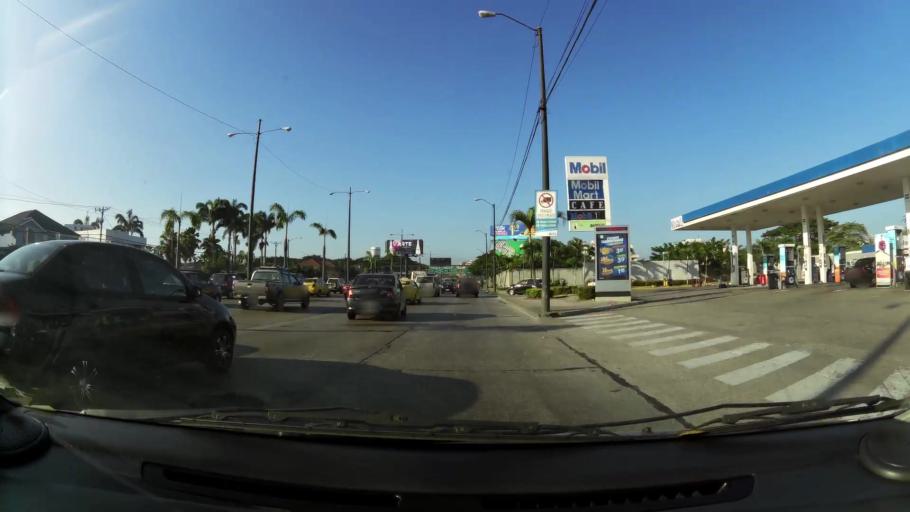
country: EC
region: Guayas
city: Eloy Alfaro
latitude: -2.1641
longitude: -79.8802
